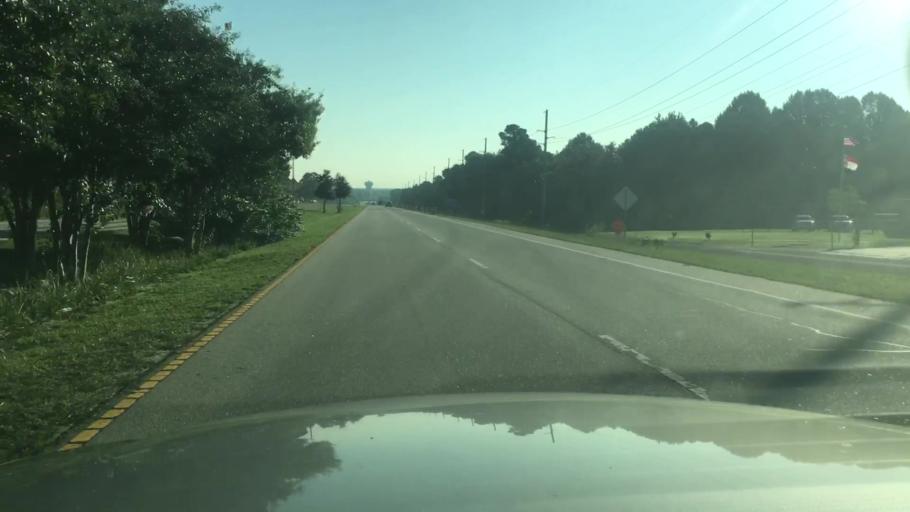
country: US
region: North Carolina
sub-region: Cumberland County
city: Fayetteville
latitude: 35.0230
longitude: -78.8926
